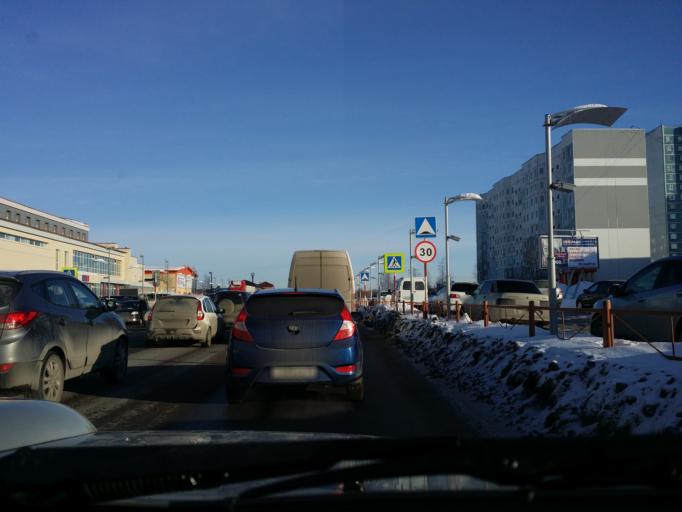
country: RU
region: Khanty-Mansiyskiy Avtonomnyy Okrug
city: Nizhnevartovsk
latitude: 60.9498
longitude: 76.6131
